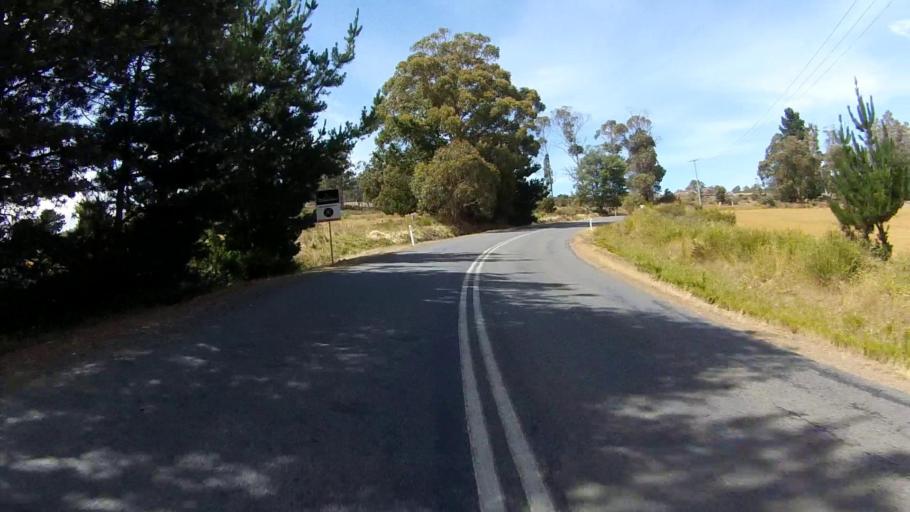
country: AU
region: Tasmania
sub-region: Huon Valley
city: Cygnet
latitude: -43.2170
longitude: 147.1223
